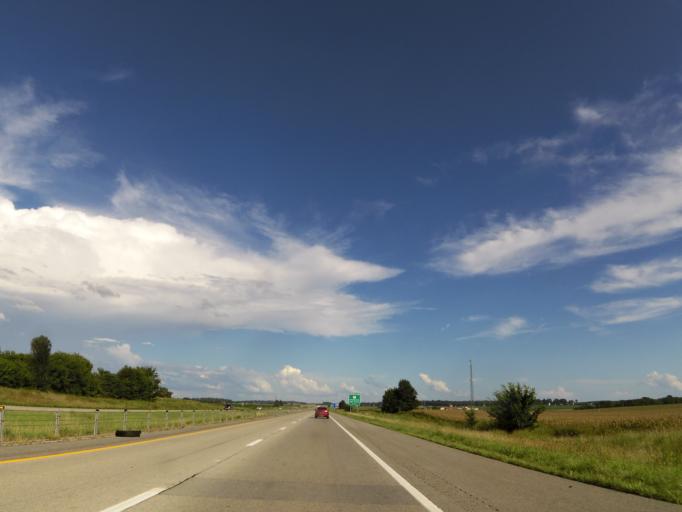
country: US
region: Kentucky
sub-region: Christian County
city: Oak Grove
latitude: 36.6874
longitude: -87.4166
